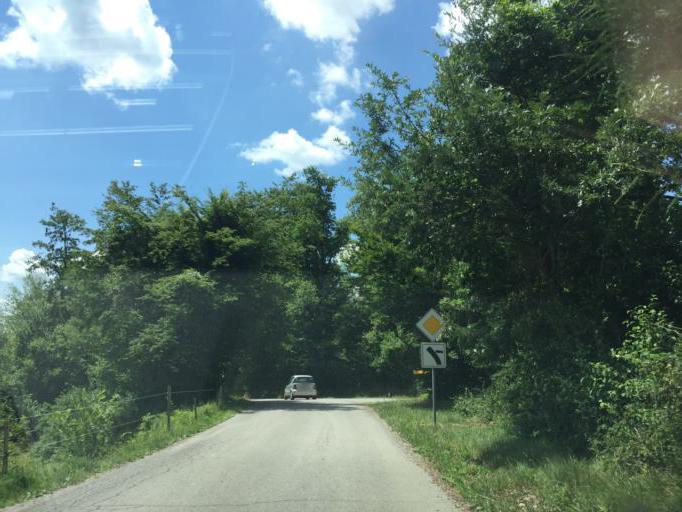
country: SI
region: Postojna
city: Postojna
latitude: 45.8070
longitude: 14.1476
